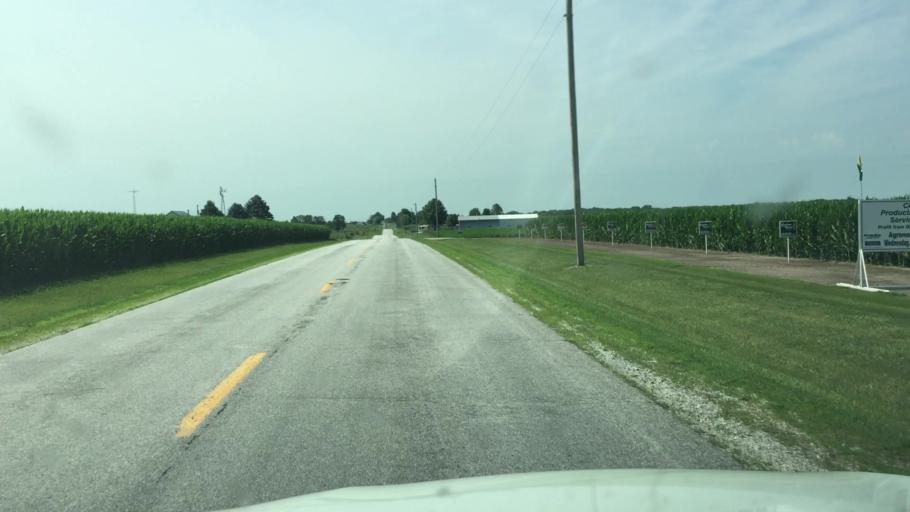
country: US
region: Illinois
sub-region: Hancock County
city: Nauvoo
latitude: 40.5052
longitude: -91.3086
